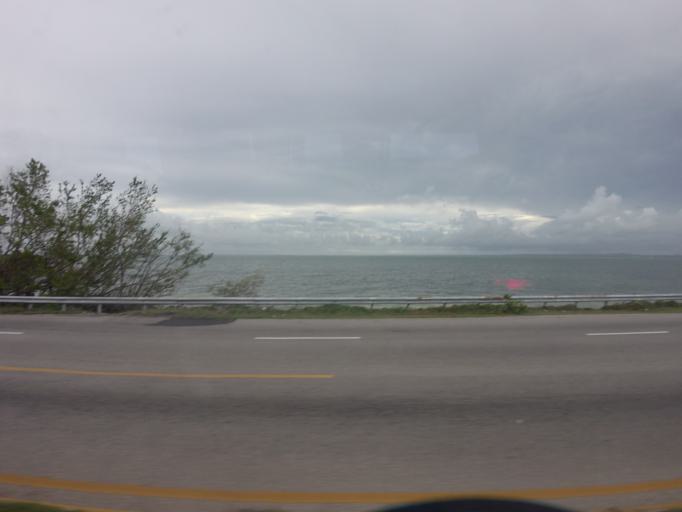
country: CU
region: Matanzas
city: Varadero
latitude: 23.1716
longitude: -81.2095
